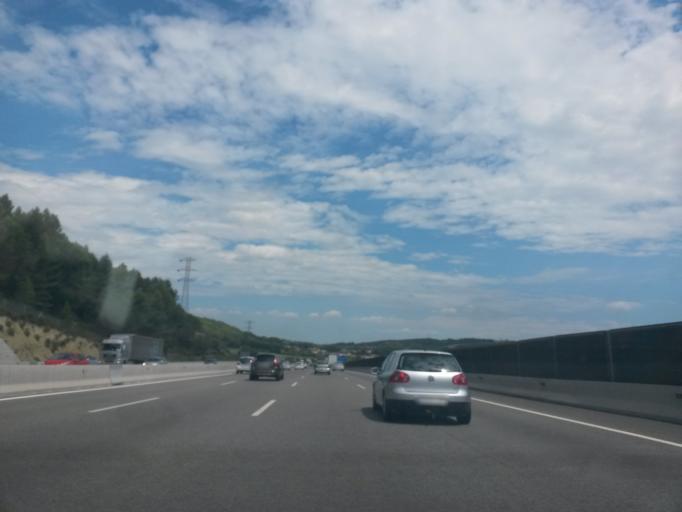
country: ES
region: Catalonia
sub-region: Provincia de Girona
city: Sarria de Ter
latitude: 42.0165
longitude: 2.8142
